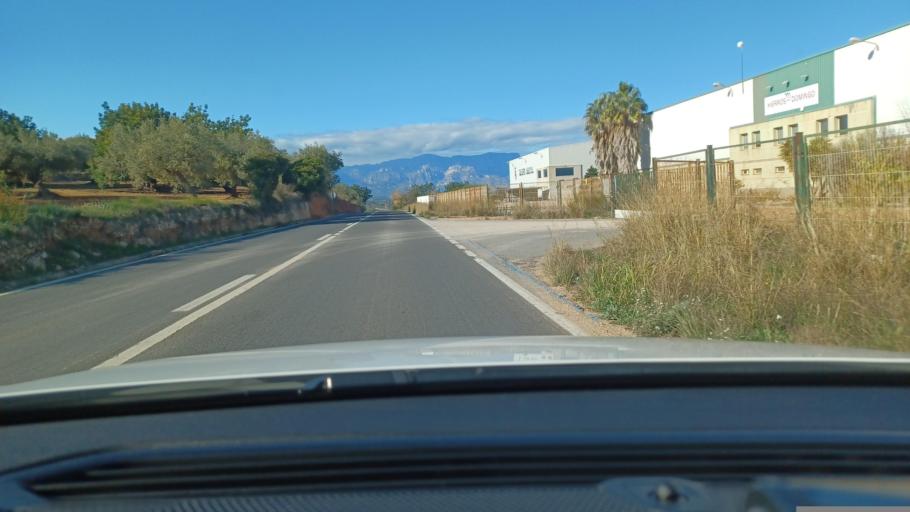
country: ES
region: Catalonia
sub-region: Provincia de Tarragona
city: Masdenverge
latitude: 40.7097
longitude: 0.5395
